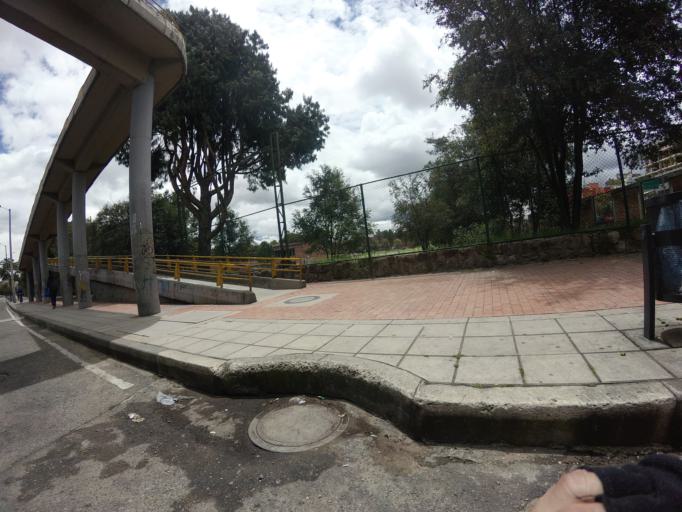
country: CO
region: Bogota D.C.
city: Barrio San Luis
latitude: 4.7037
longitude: -74.0332
